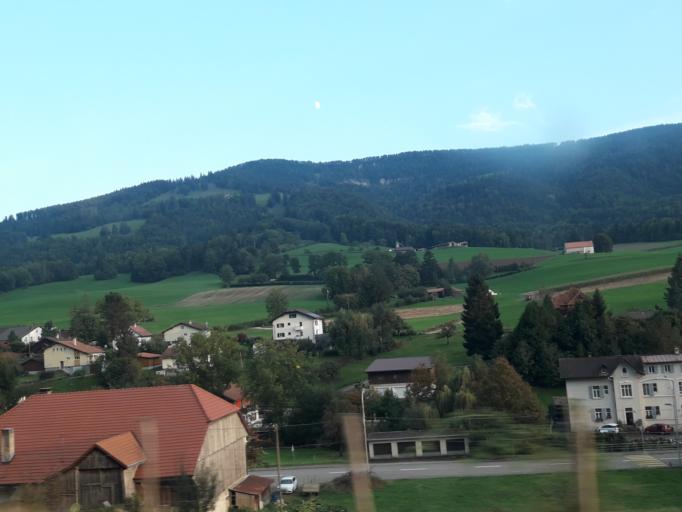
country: CH
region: Bern
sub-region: Jura bernois
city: Moutier
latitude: 47.2836
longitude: 7.4215
